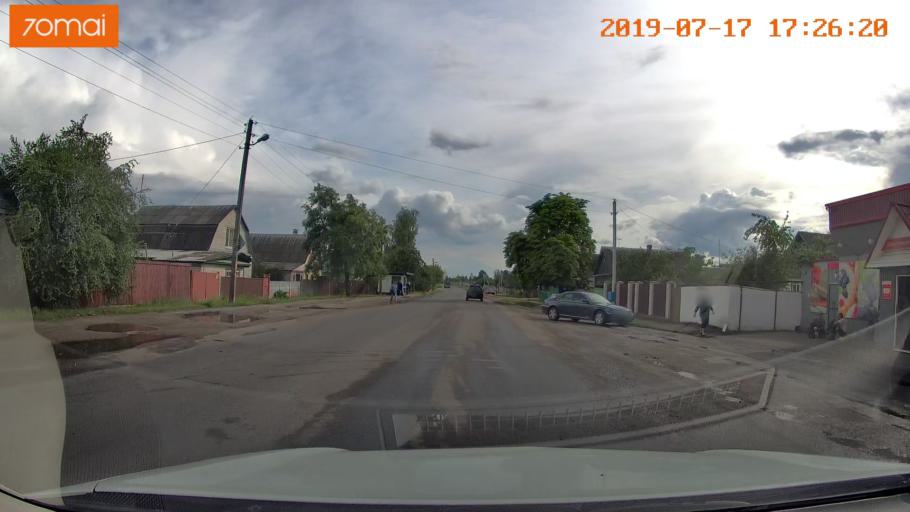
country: BY
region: Mogilev
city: Babruysk
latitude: 53.1420
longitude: 29.1726
